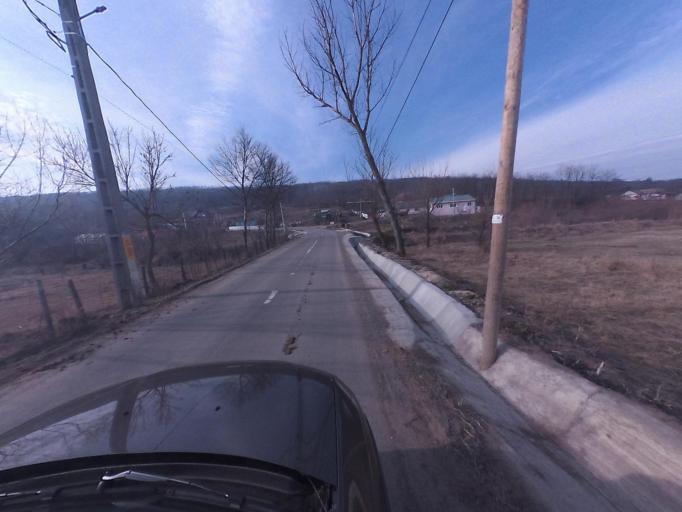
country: RO
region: Vaslui
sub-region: Comuna Solesti
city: Solesti
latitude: 46.8078
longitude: 27.7769
